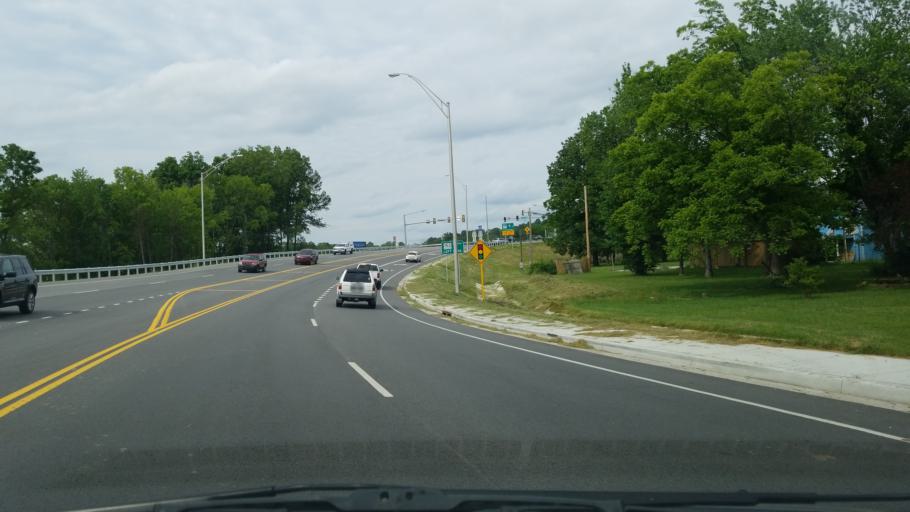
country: US
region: Tennessee
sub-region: Hamilton County
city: East Brainerd
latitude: 35.0411
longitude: -85.1884
